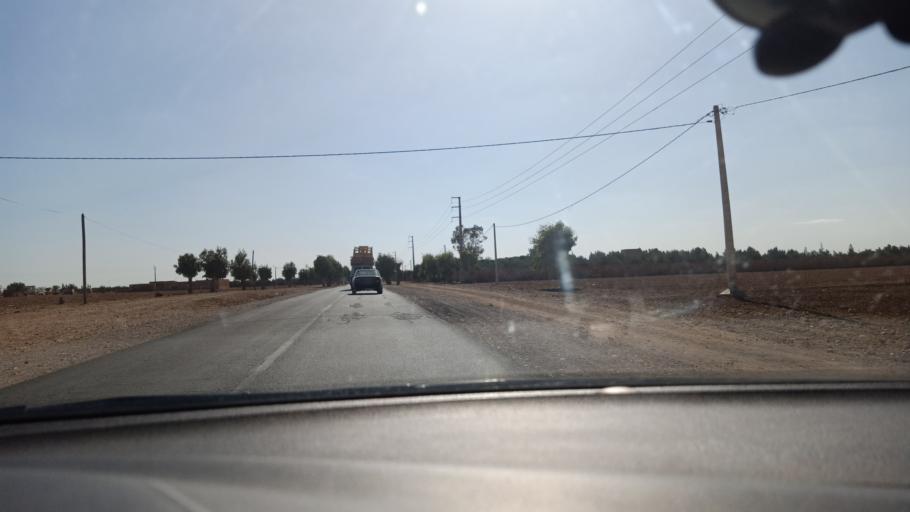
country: MA
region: Doukkala-Abda
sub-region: Safi
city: Youssoufia
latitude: 32.0965
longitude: -8.6146
